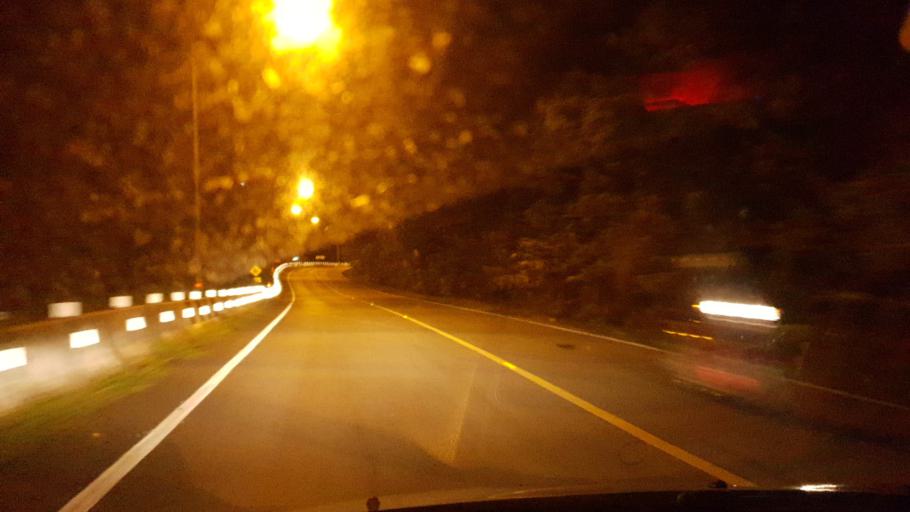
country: TH
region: Mae Hong Son
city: Khun Yuam
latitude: 18.7443
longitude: 97.9269
